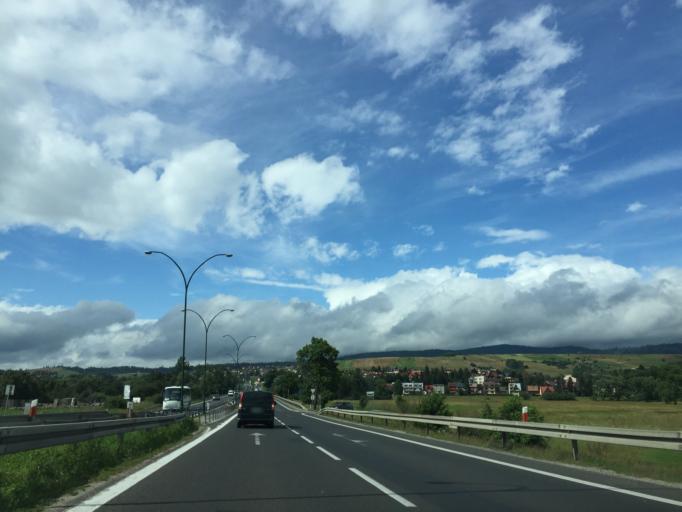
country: PL
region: Lesser Poland Voivodeship
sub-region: Powiat nowotarski
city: Nowy Targ
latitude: 49.4817
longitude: 20.0209
